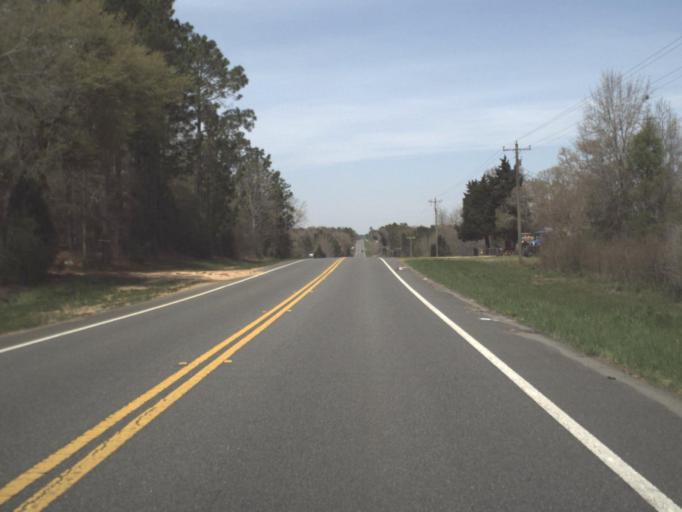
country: US
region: Alabama
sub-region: Geneva County
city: Geneva
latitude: 30.8717
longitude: -85.9466
